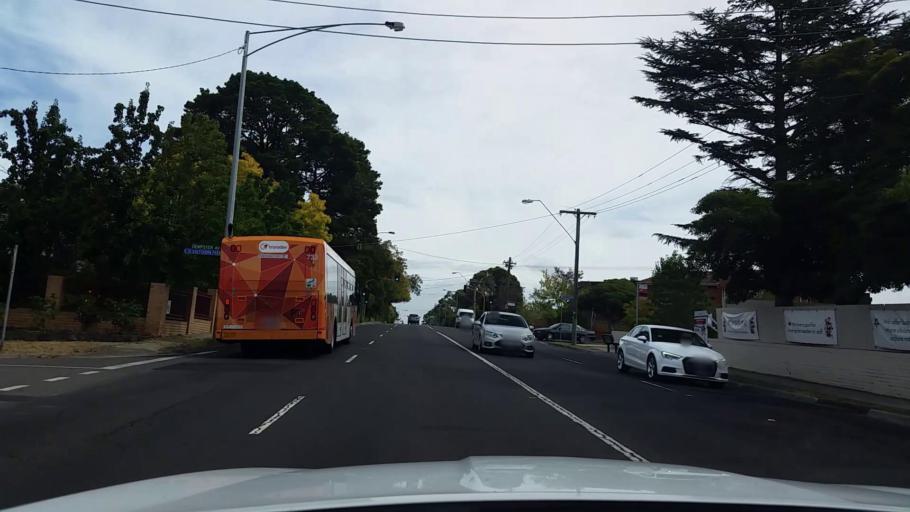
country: AU
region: Victoria
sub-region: Boroondara
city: Balwyn North
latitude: -37.7928
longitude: 145.0906
